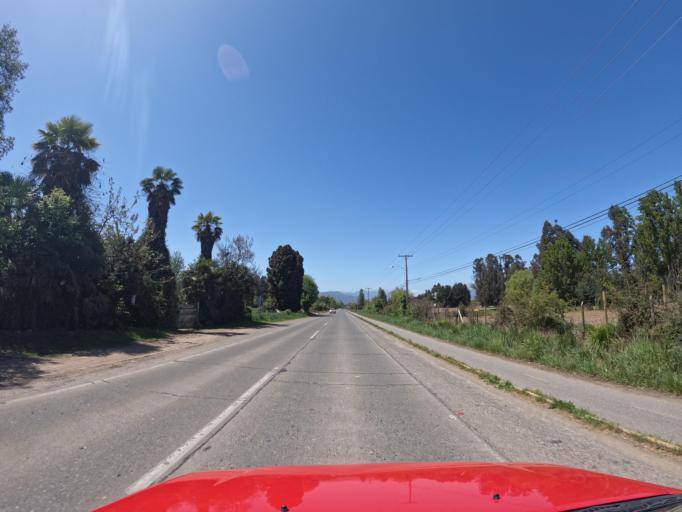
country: CL
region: Maule
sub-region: Provincia de Linares
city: Linares
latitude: -35.8297
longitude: -71.5085
